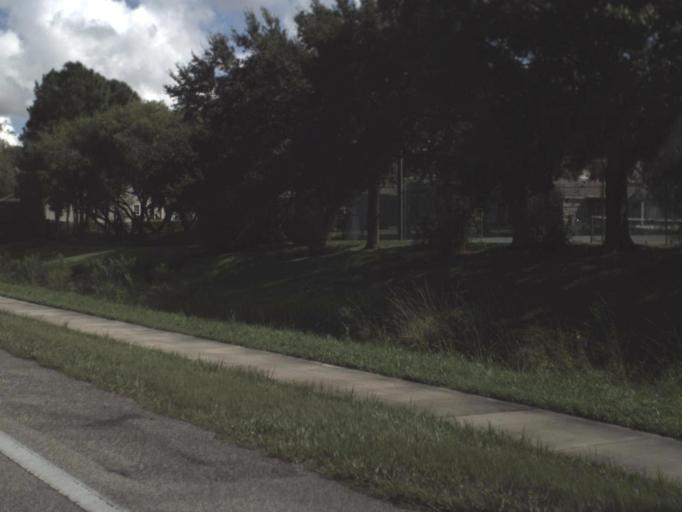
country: US
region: Florida
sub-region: Polk County
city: Medulla
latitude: 28.0059
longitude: -81.9748
